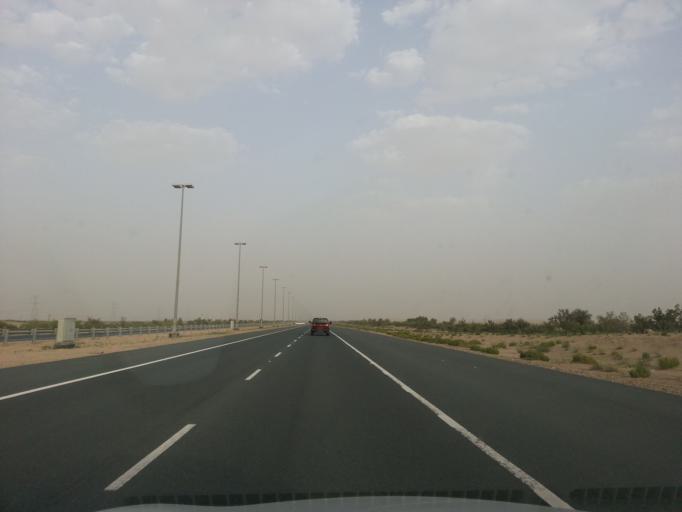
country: AE
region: Dubai
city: Dubai
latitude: 24.5920
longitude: 55.1445
